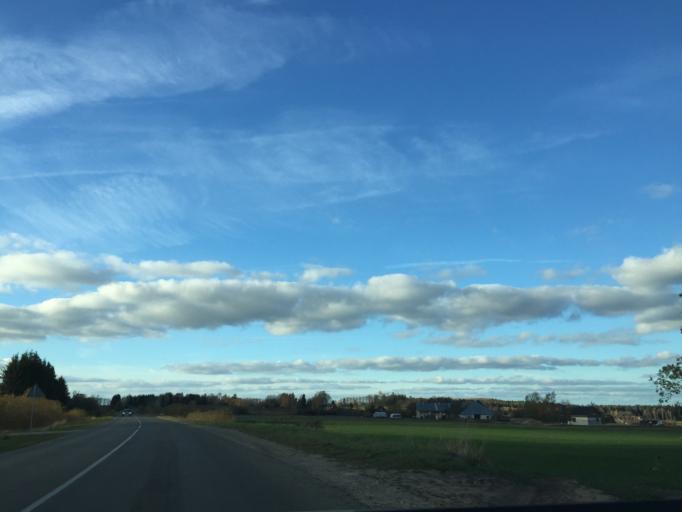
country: LV
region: Tukuma Rajons
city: Tukums
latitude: 56.9900
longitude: 23.0983
